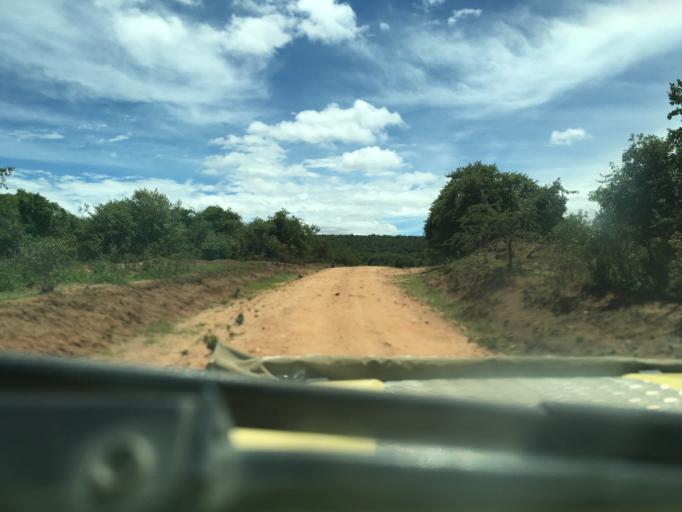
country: TZ
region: Mara
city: Mugumu
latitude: -1.8927
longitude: 35.3910
